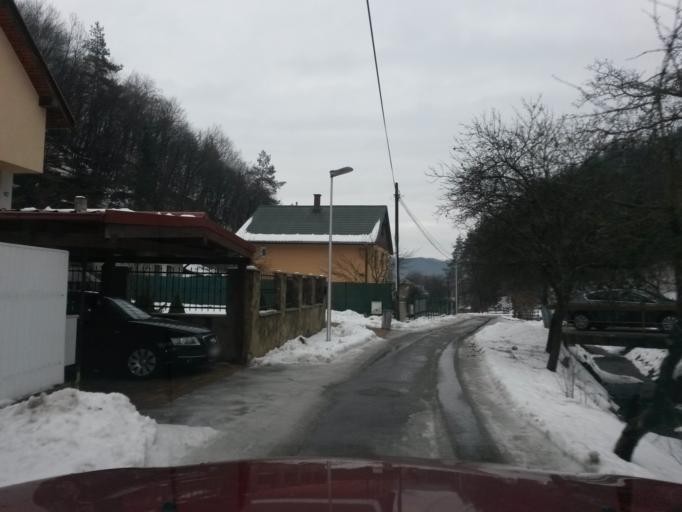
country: SK
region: Kosicky
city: Kosice
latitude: 48.7939
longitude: 21.2350
